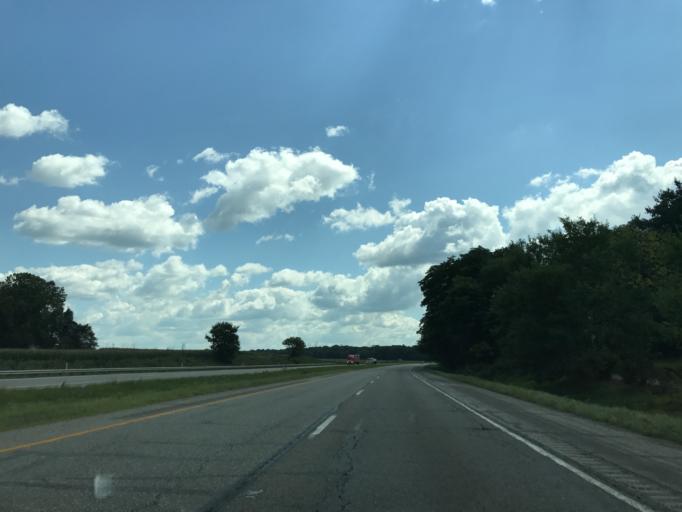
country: US
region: Indiana
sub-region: Marshall County
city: Plymouth
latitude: 41.3601
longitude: -86.2912
